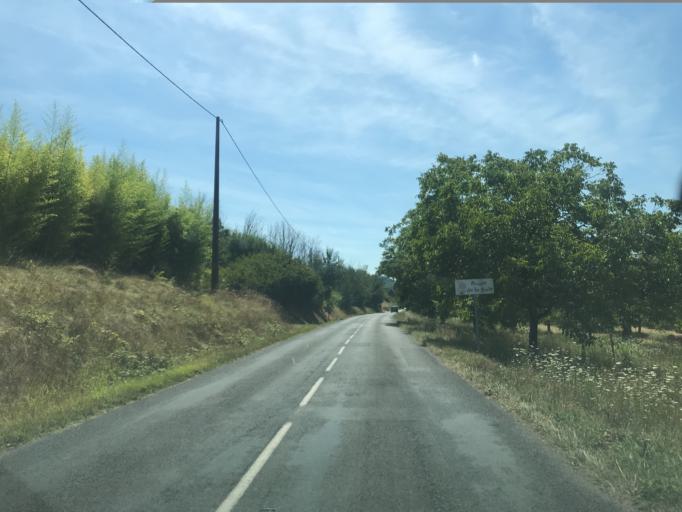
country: FR
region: Aquitaine
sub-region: Departement de la Dordogne
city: Cenac-et-Saint-Julien
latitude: 44.8173
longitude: 1.1925
